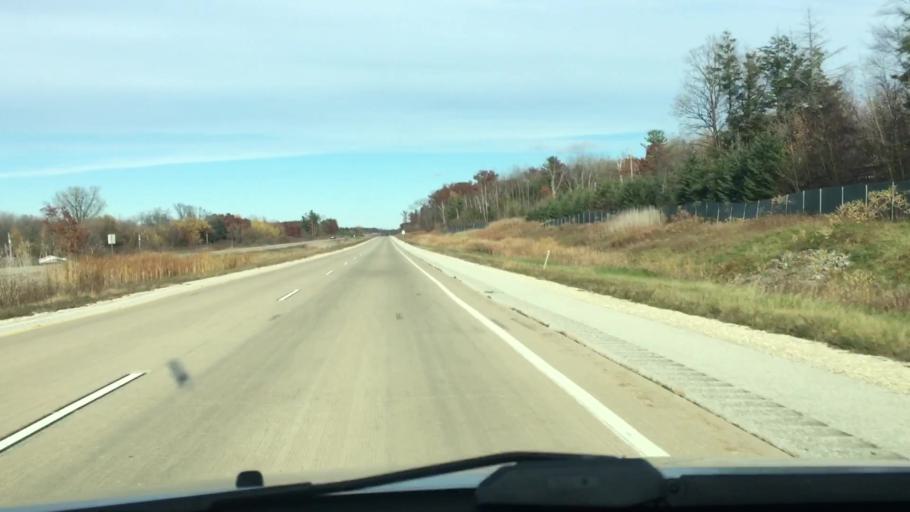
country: US
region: Wisconsin
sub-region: Kewaunee County
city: Luxemburg
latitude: 44.6898
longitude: -87.7184
